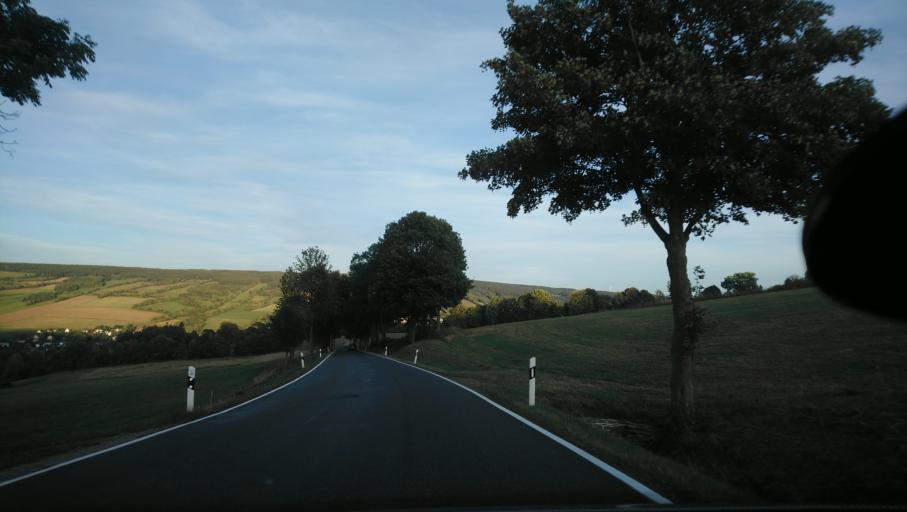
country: DE
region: Saxony
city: Konigswalde
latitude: 50.5474
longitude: 13.0251
